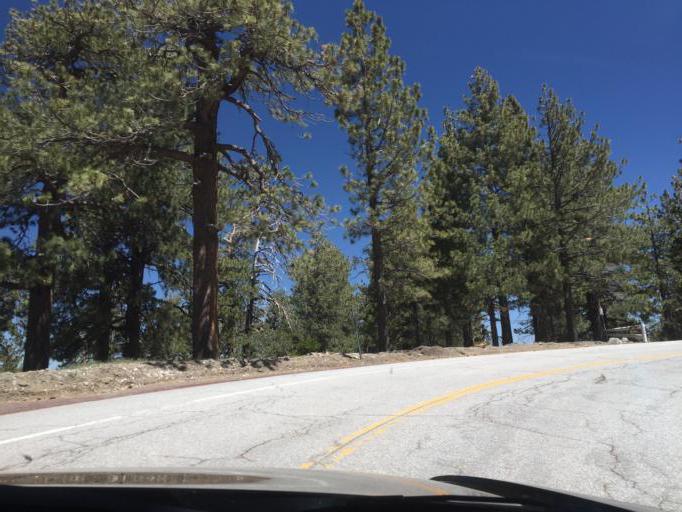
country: US
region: California
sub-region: San Bernardino County
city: Wrightwood
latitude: 34.3858
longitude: -117.6893
